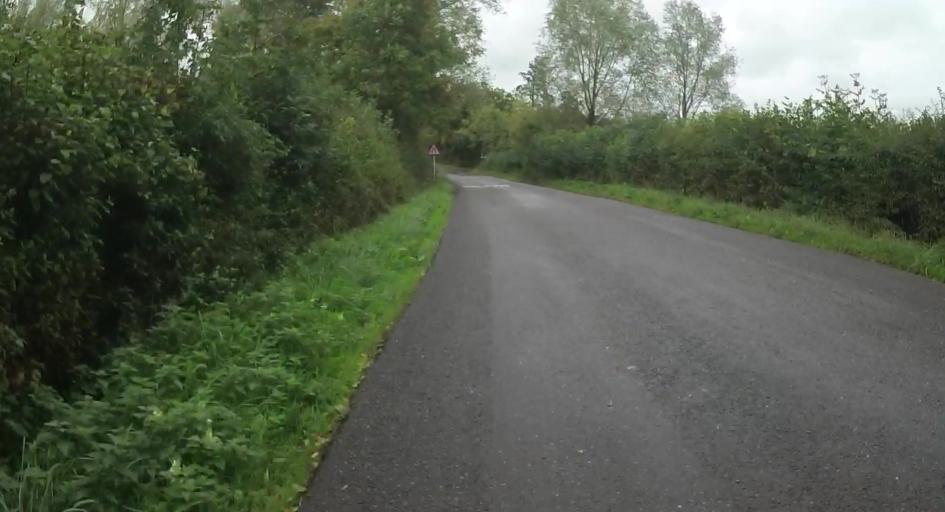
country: GB
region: England
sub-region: Hampshire
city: Tadley
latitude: 51.3069
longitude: -1.1522
